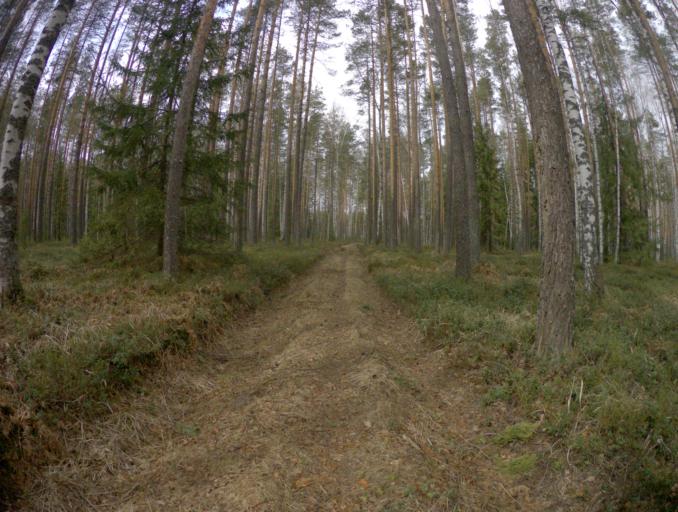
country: RU
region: Vladimir
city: Raduzhnyy
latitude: 55.9491
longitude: 40.2853
